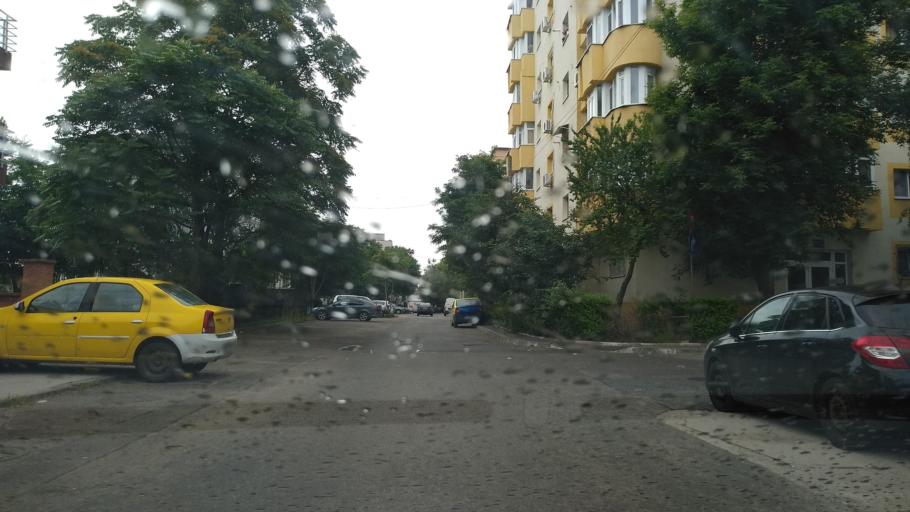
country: RO
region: Ilfov
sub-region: Comuna Fundeni-Dobroesti
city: Fundeni
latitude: 44.4602
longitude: 26.1381
